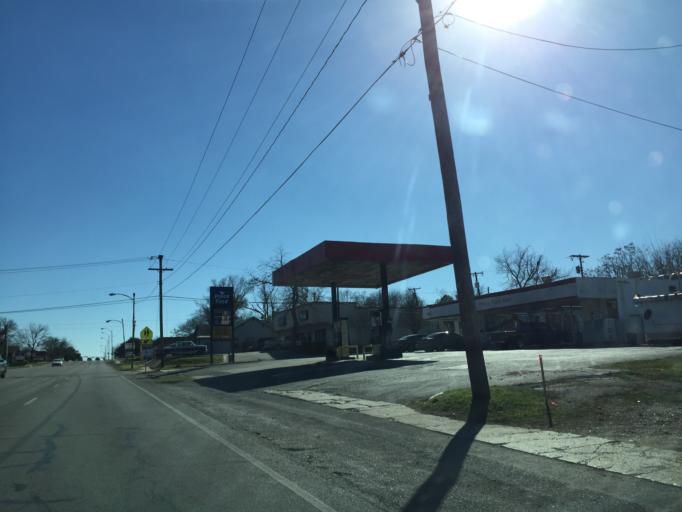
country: US
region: Texas
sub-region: Williamson County
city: Taylor
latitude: 30.5777
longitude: -97.4105
